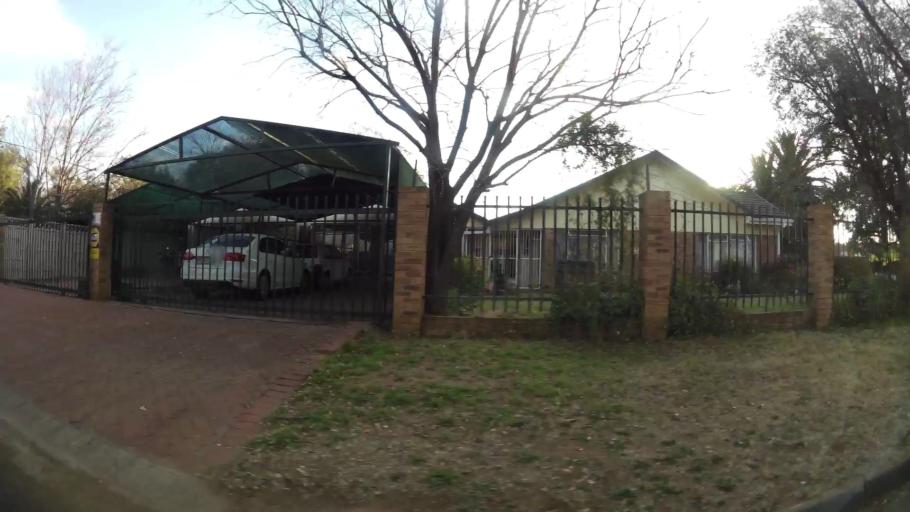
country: ZA
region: Orange Free State
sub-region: Mangaung Metropolitan Municipality
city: Bloemfontein
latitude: -29.1354
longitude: 26.1884
